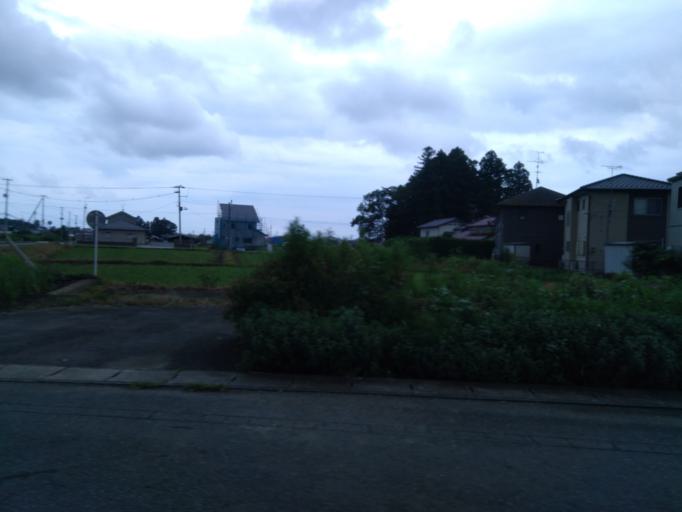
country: JP
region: Fukushima
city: Namie
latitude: 37.6340
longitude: 140.9285
